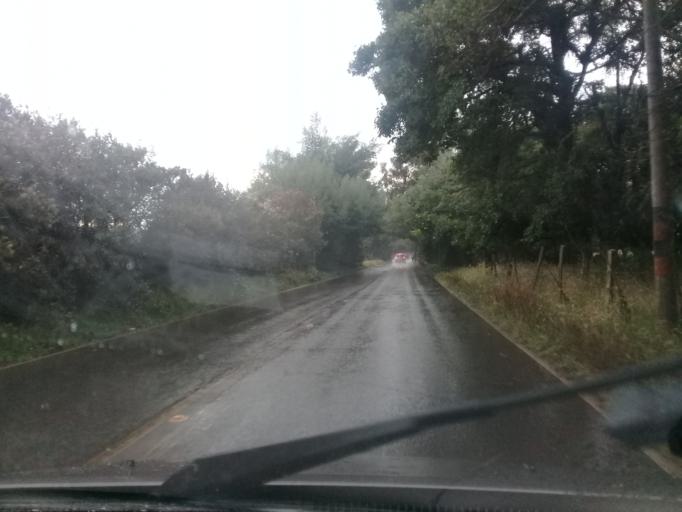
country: CO
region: Cundinamarca
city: Guasca
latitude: 4.8521
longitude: -73.8509
